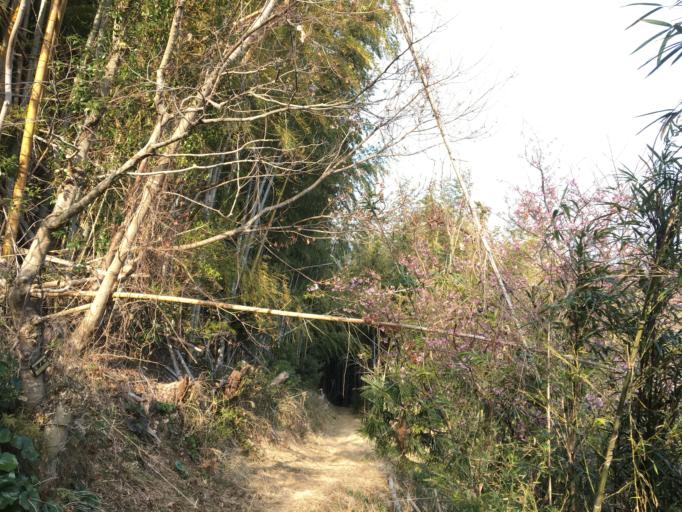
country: JP
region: Shizuoka
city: Shimoda
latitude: 34.7519
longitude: 138.9970
